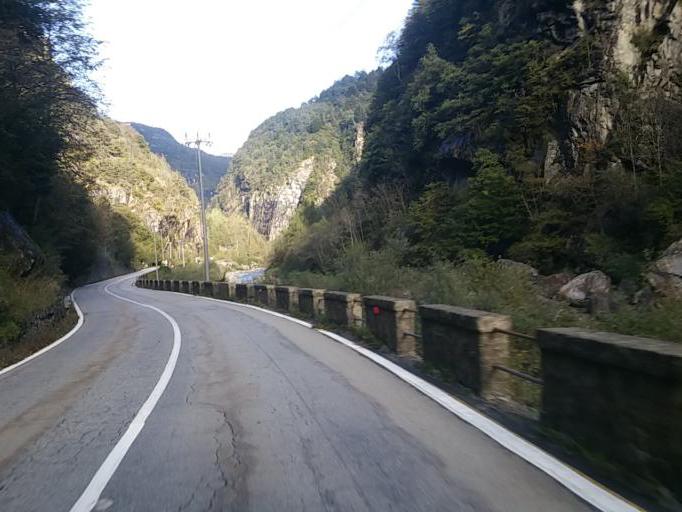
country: IT
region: Piedmont
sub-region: Provincia Verbano-Cusio-Ossola
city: Trasquera
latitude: 46.2008
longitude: 8.1757
